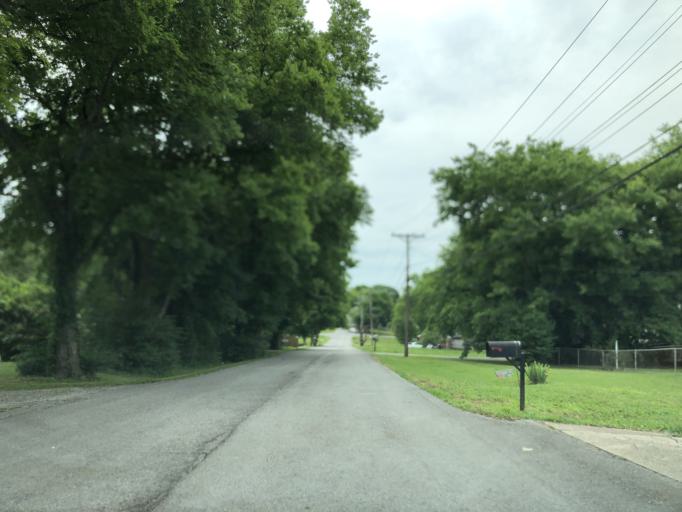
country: US
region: Tennessee
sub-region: Davidson County
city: Goodlettsville
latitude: 36.2885
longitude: -86.7122
